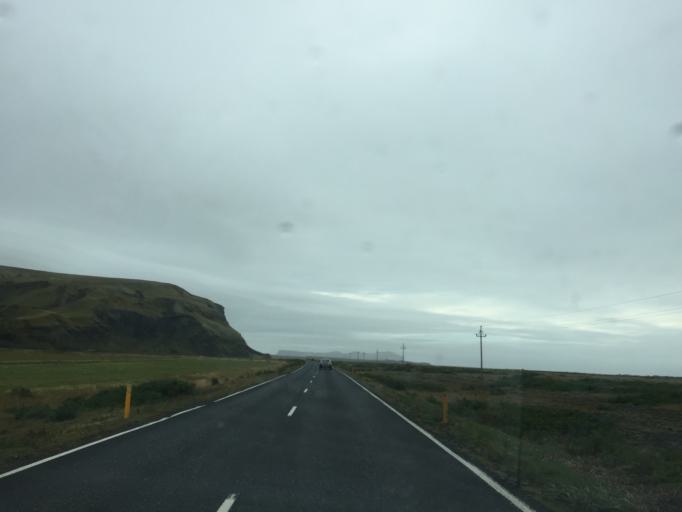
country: IS
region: South
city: Vestmannaeyjar
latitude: 63.4190
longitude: -18.9578
